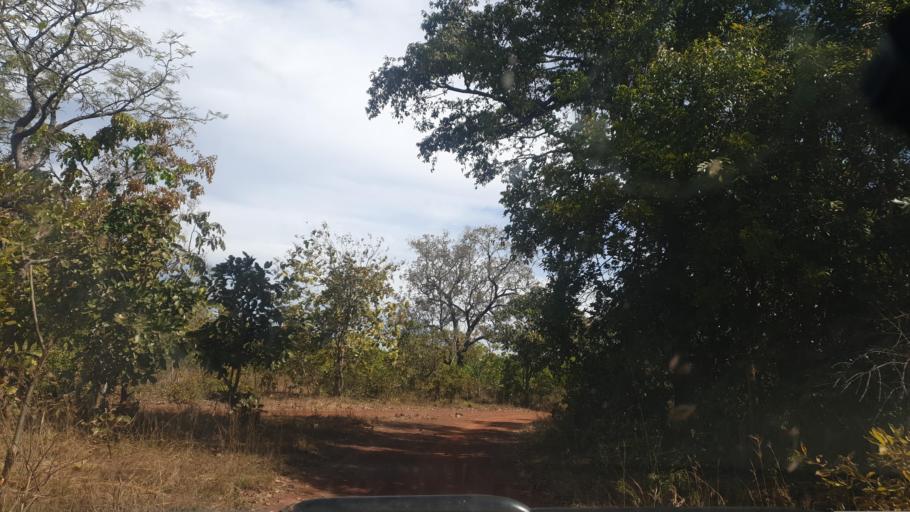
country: ML
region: Sikasso
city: Yanfolila
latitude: 10.4978
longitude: -7.9600
